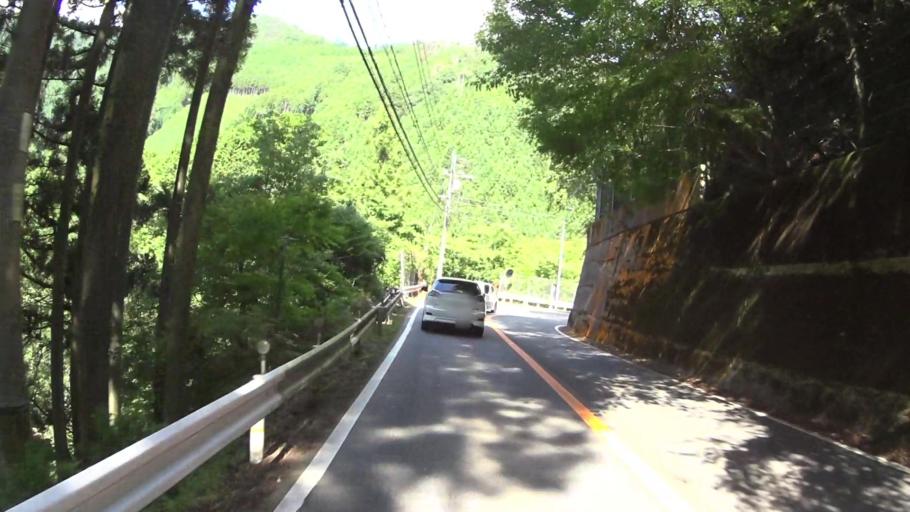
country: JP
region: Kyoto
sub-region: Kyoto-shi
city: Kamigyo-ku
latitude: 35.0991
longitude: 135.6884
